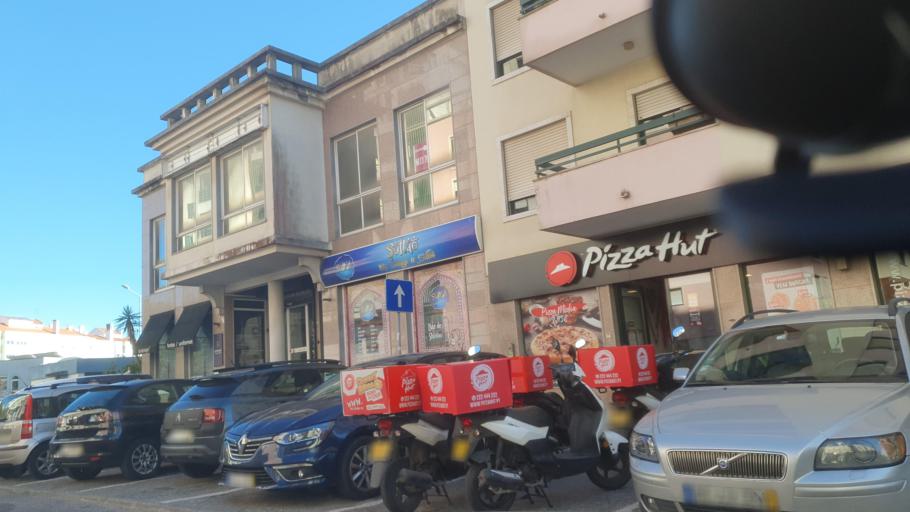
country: PT
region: Lisbon
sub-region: Oeiras
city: Barcarena
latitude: 38.7523
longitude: -9.2795
